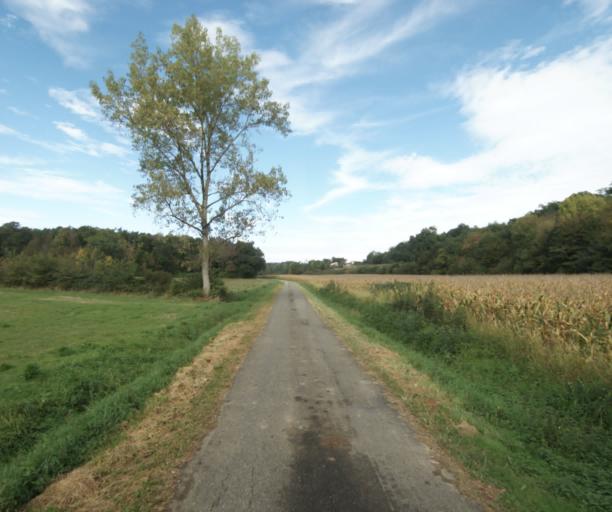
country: FR
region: Aquitaine
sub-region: Departement des Landes
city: Villeneuve-de-Marsan
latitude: 43.9014
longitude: -0.2175
